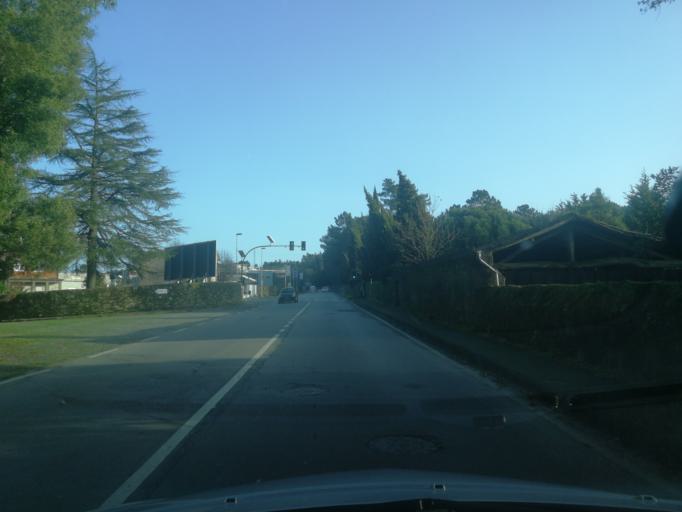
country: PT
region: Braga
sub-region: Barcelos
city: Barcelos
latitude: 41.5250
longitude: -8.6142
